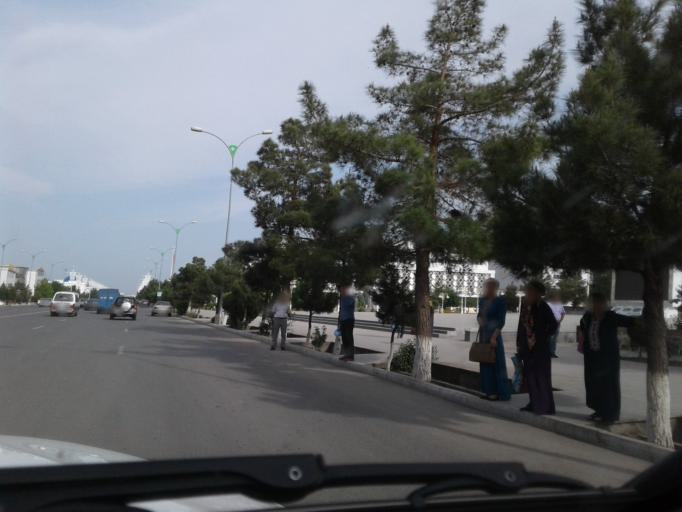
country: TM
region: Mary
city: Mary
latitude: 37.5948
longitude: 61.8350
